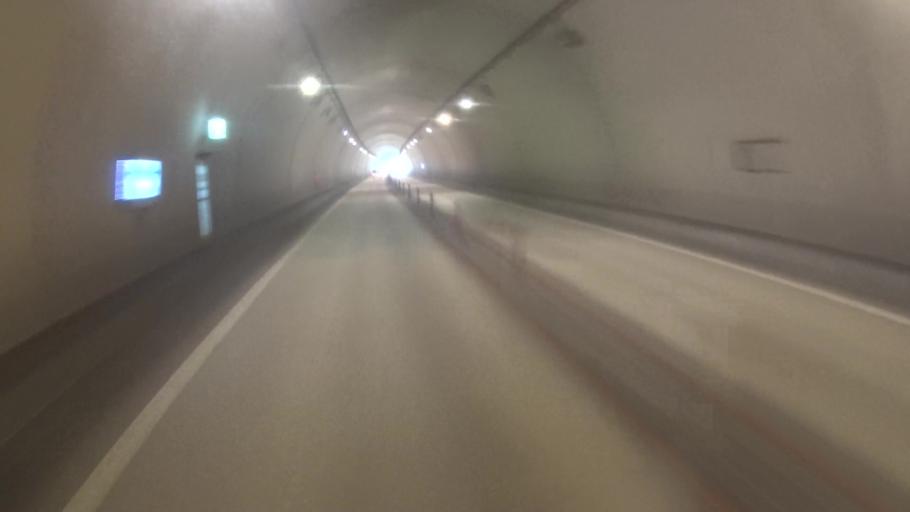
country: JP
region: Kyoto
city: Miyazu
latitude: 35.5449
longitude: 135.1531
